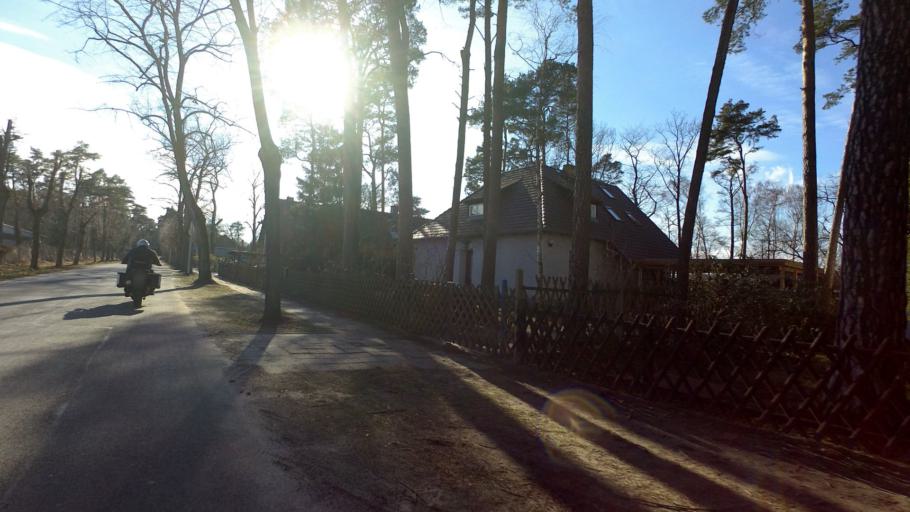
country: DE
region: Brandenburg
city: Oranienburg
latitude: 52.7545
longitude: 13.2740
